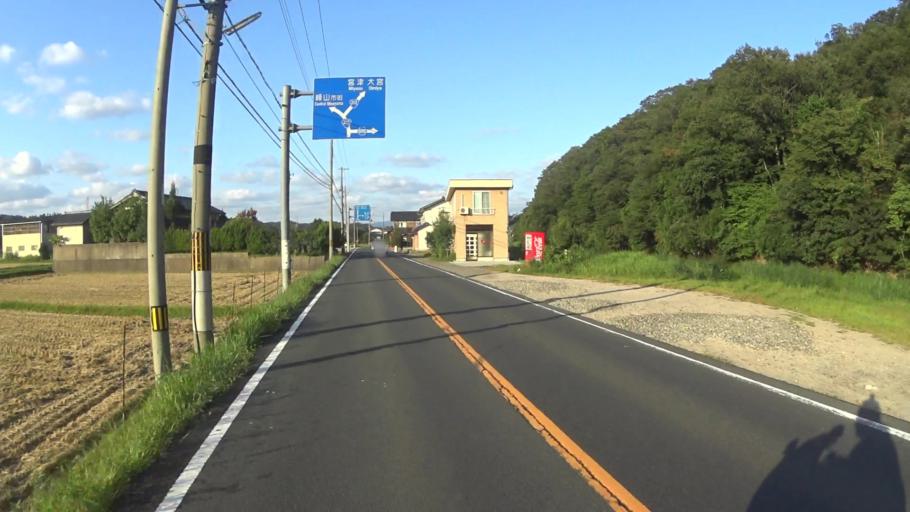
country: JP
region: Kyoto
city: Miyazu
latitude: 35.5974
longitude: 135.0447
